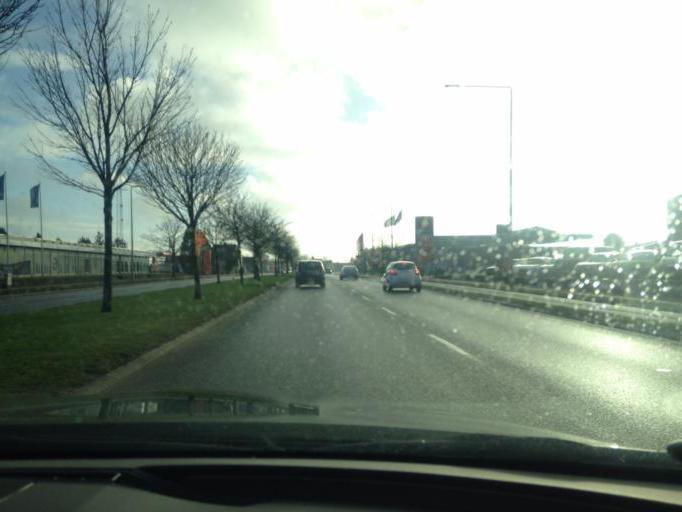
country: DK
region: South Denmark
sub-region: Kolding Kommune
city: Kolding
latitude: 55.5062
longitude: 9.4571
